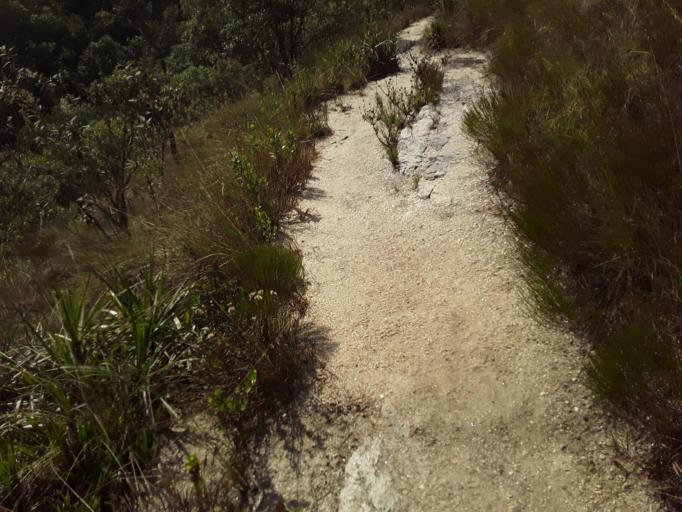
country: BR
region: Minas Gerais
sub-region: Lima Duarte
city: Lima Duarte
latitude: -21.6984
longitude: -43.8843
